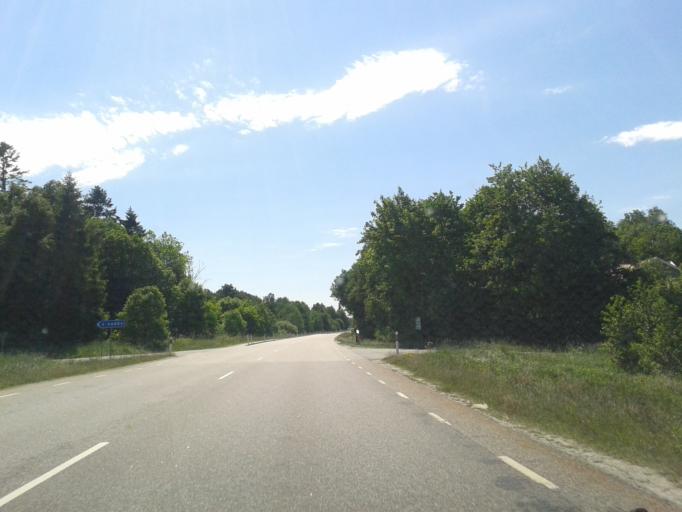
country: SE
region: Vaestra Goetaland
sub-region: Stenungsunds Kommun
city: Stora Hoga
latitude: 58.0420
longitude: 11.8910
